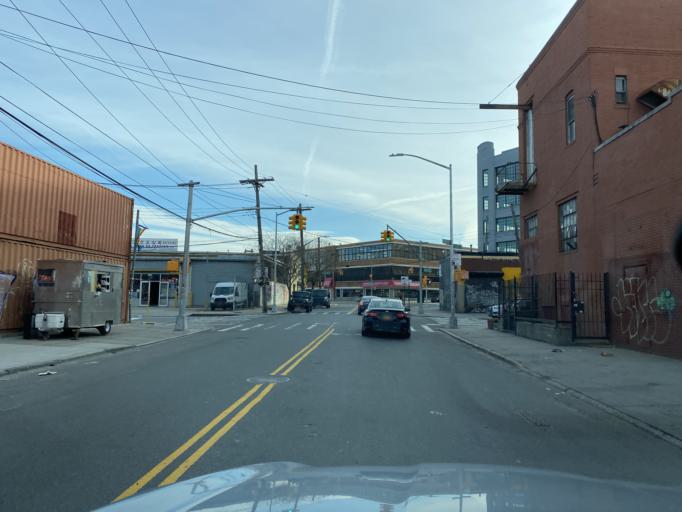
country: US
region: New York
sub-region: Queens County
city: Long Island City
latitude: 40.7093
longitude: -73.9229
